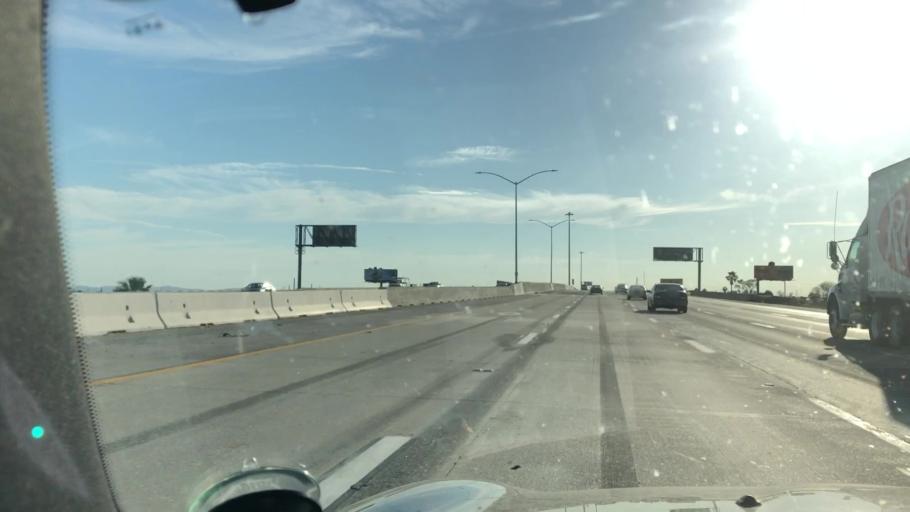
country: US
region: California
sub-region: Riverside County
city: Mira Loma
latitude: 34.0183
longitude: -117.5231
